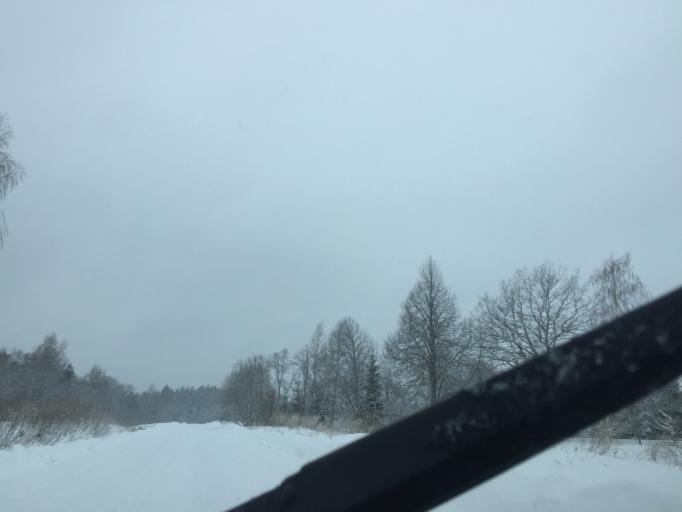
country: LV
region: Amatas Novads
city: Drabesi
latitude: 57.1669
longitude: 25.3044
